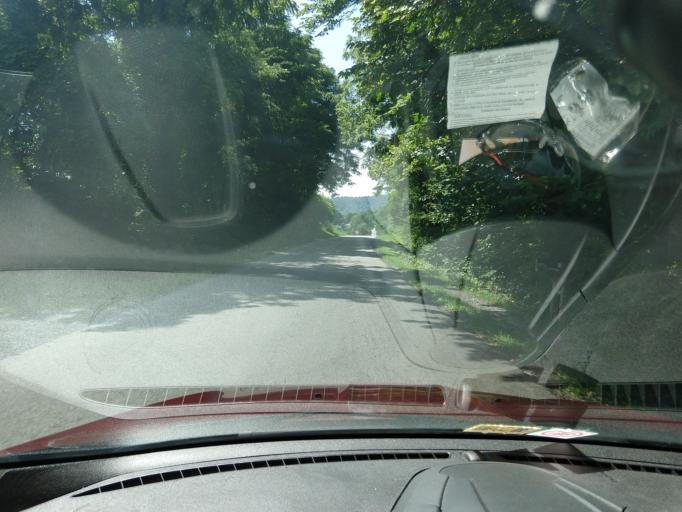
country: US
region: Virginia
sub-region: Rockingham County
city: Broadway
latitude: 38.5716
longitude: -78.8876
